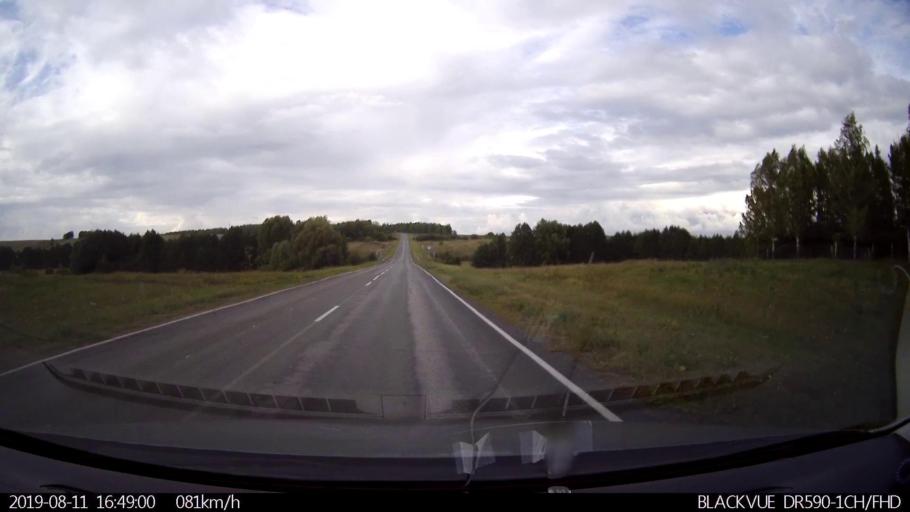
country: RU
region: Ulyanovsk
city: Mayna
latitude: 54.2159
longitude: 47.6943
